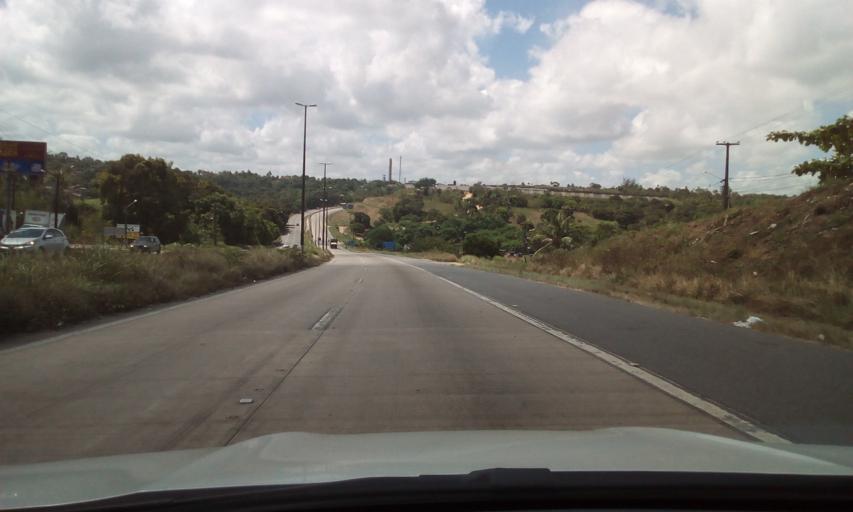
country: BR
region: Pernambuco
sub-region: Igarassu
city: Igarassu
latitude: -7.8101
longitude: -34.9206
